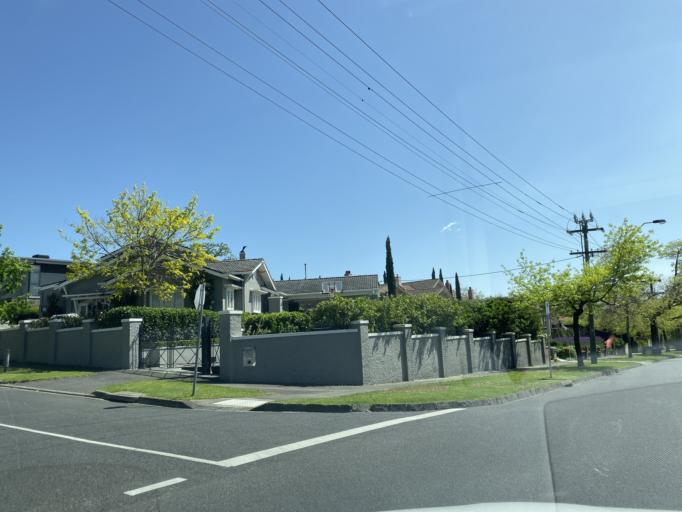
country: AU
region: Victoria
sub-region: Boroondara
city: Camberwell
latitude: -37.8464
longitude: 145.0688
